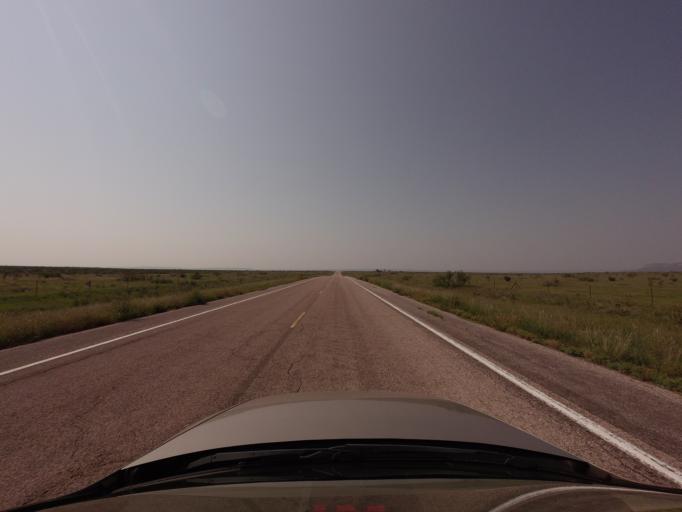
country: US
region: New Mexico
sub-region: Quay County
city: Tucumcari
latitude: 34.9627
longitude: -103.7558
